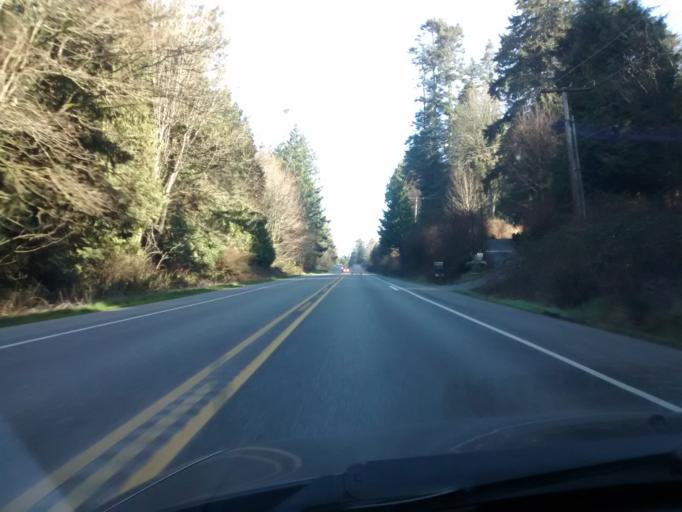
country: US
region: Washington
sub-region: Kitsap County
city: Lofall
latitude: 47.8357
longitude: -122.6210
